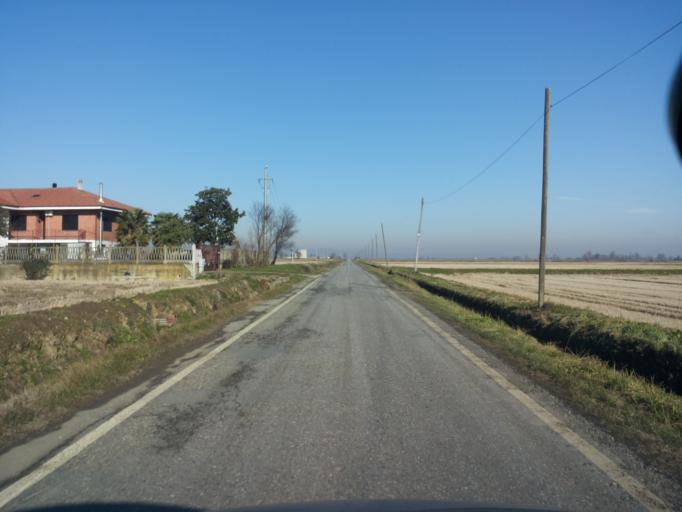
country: IT
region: Piedmont
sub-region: Provincia di Vercelli
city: Formigliana
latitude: 45.4115
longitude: 8.2479
